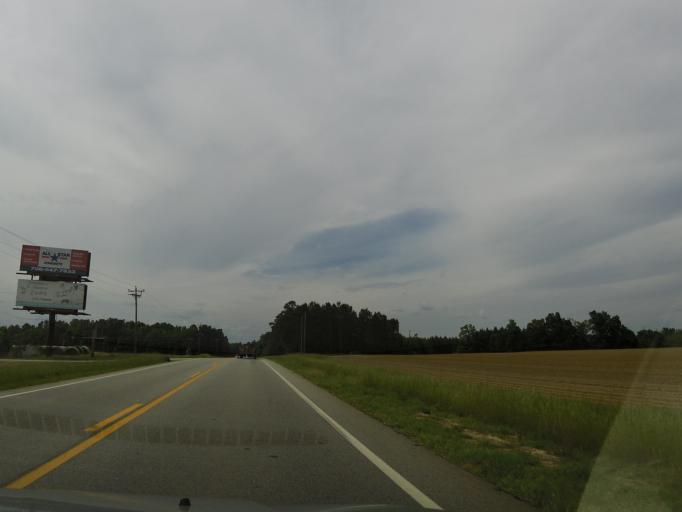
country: US
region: Georgia
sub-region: Jefferson County
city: Wrens
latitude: 33.2366
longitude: -82.4088
